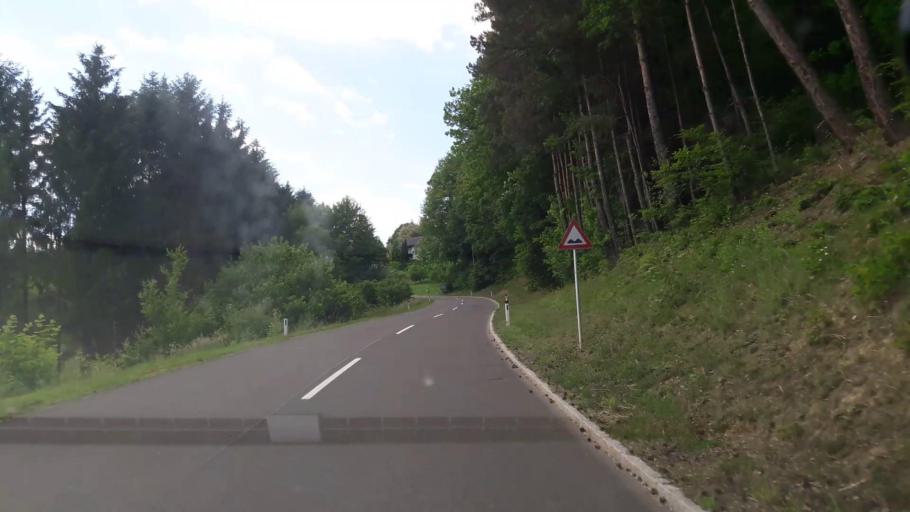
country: AT
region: Burgenland
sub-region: Politischer Bezirk Jennersdorf
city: Neuhaus am Klausenbach
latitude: 46.8726
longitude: 16.0483
